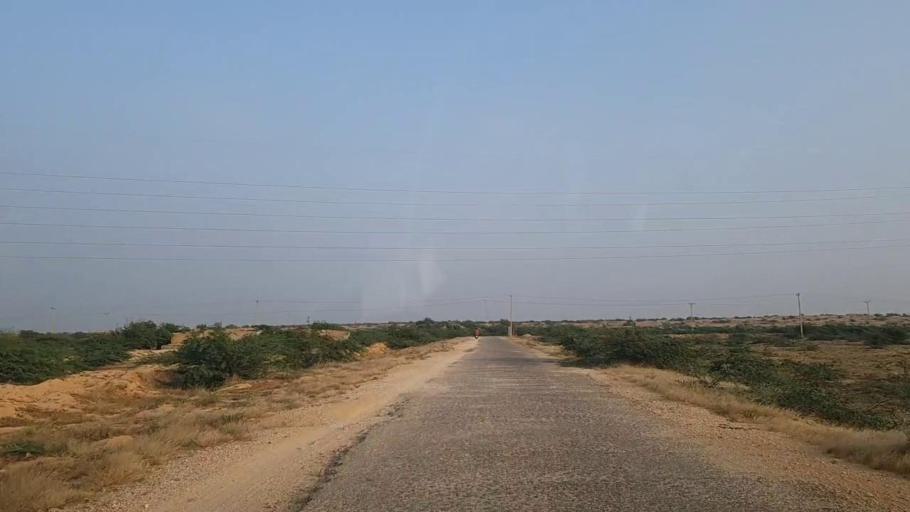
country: PK
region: Sindh
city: Thatta
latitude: 24.6887
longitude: 67.8512
